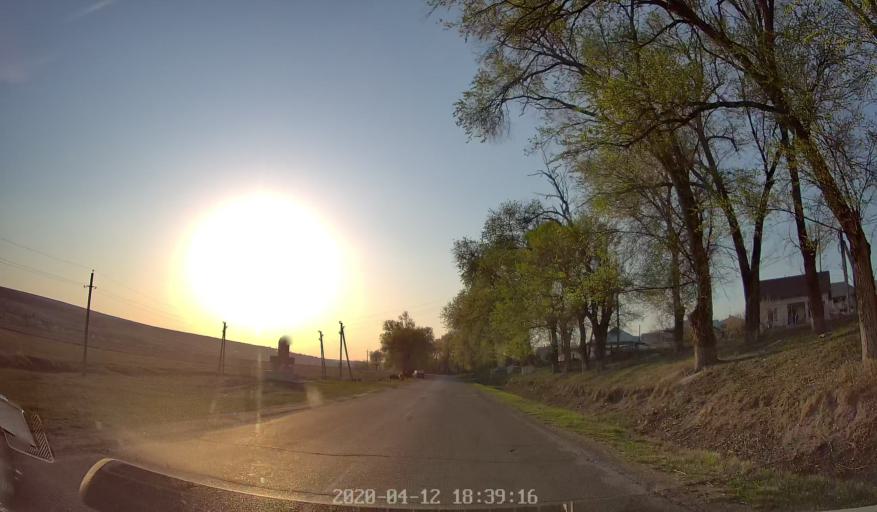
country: MD
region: Chisinau
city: Vadul lui Voda
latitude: 47.1275
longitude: 28.9882
